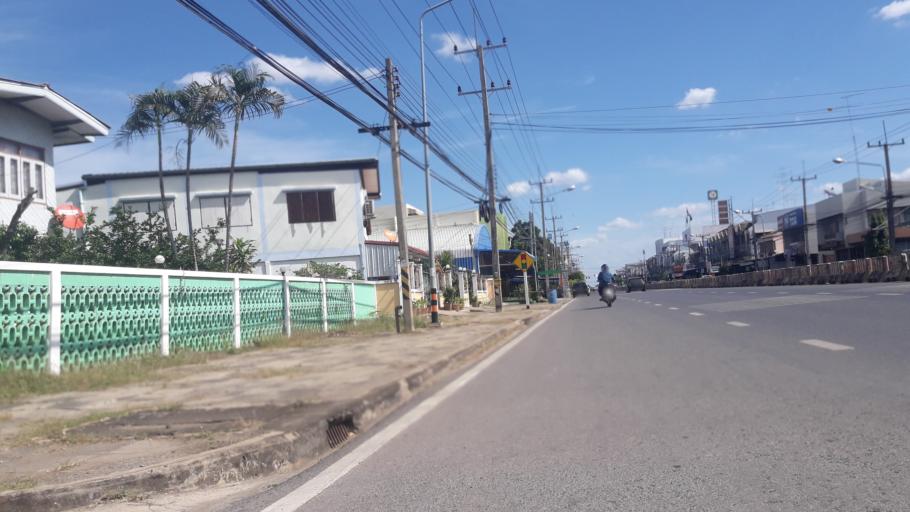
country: TH
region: Phichit
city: Thap Khlo
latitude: 16.1699
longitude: 100.5729
